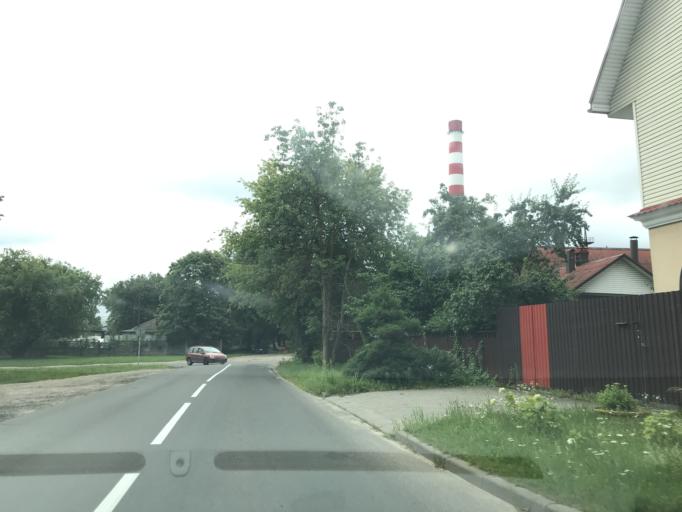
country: BY
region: Minsk
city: Minsk
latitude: 53.9353
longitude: 27.6271
